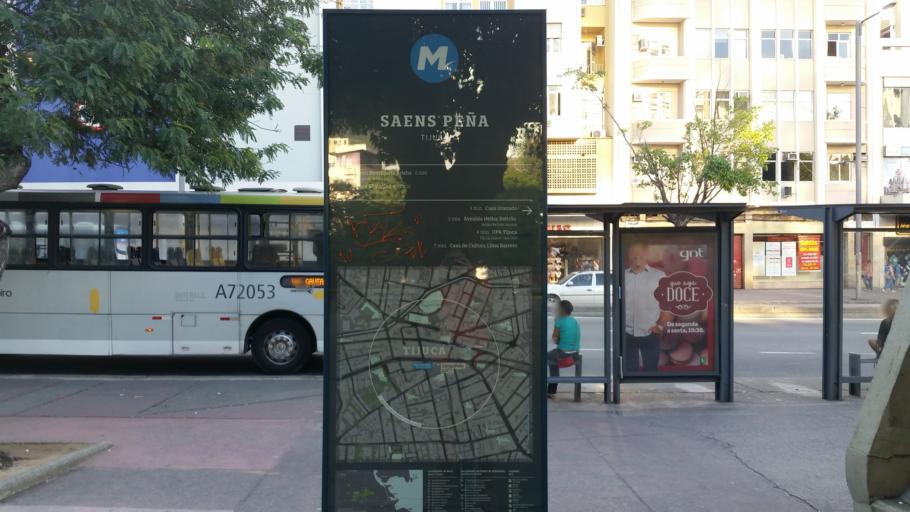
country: BR
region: Rio de Janeiro
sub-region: Rio De Janeiro
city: Rio de Janeiro
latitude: -22.9240
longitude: -43.2321
